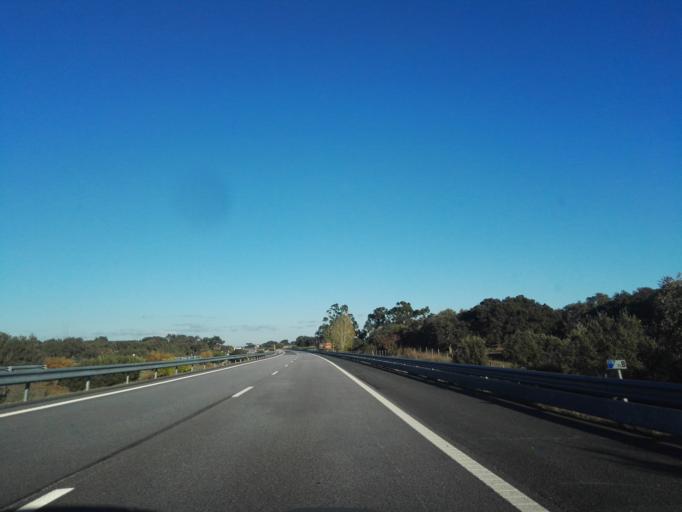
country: PT
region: Evora
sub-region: Evora
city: Evora
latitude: 38.6315
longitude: -7.8912
